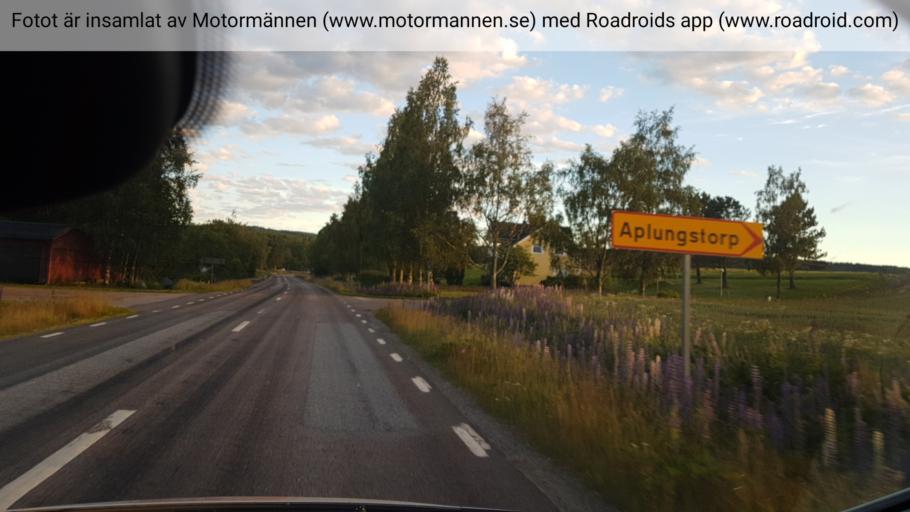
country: SE
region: Vaermland
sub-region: Sunne Kommun
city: Sunne
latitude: 59.7255
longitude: 13.1199
